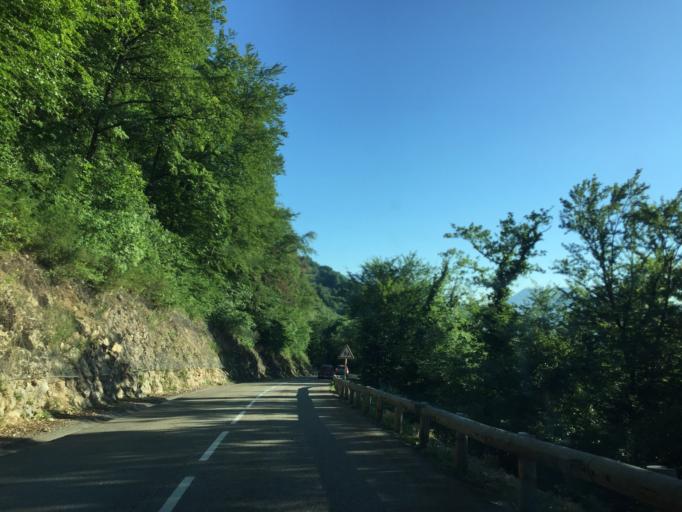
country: FR
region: Rhone-Alpes
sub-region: Departement de la Savoie
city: Challes-les-Eaux
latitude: 45.5543
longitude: 6.0271
